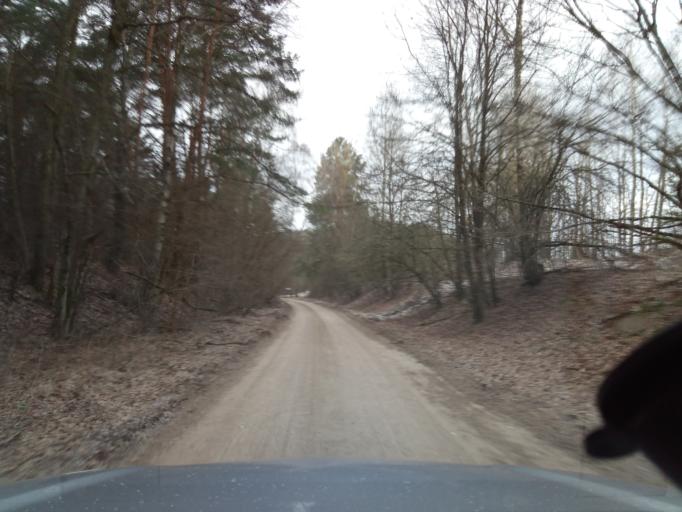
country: LT
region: Alytaus apskritis
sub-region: Alytaus rajonas
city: Daugai
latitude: 54.3166
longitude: 24.3638
